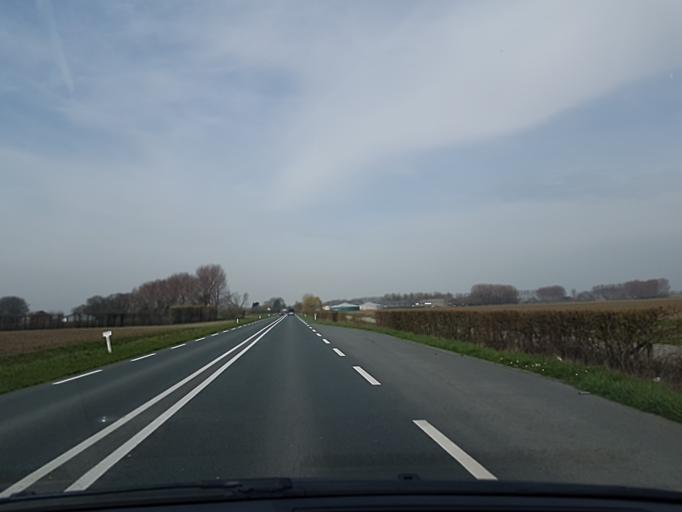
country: NL
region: Zeeland
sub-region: Gemeente Terneuzen
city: Zaamslag
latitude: 51.3157
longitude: 3.9211
